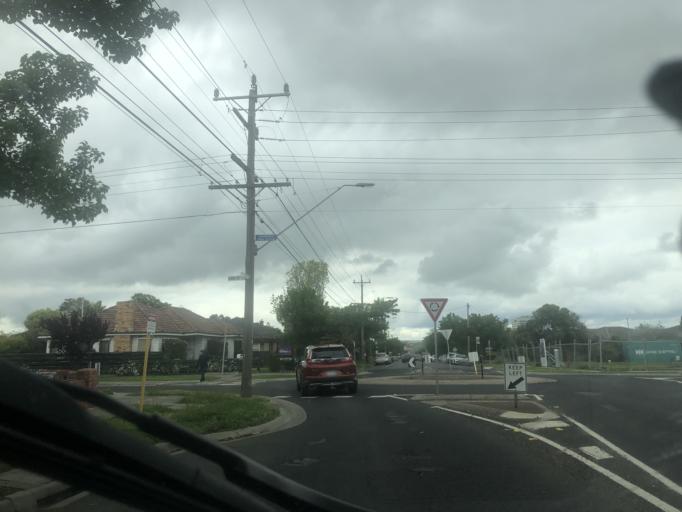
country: AU
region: Victoria
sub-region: Greater Dandenong
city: Dandenong North
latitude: -37.9786
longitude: 145.2157
